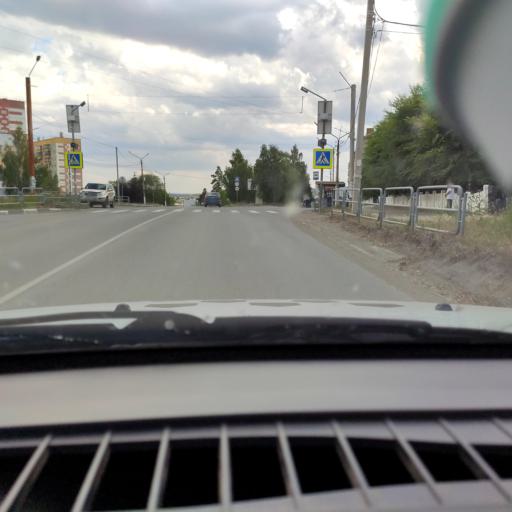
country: RU
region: Chelyabinsk
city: Miass
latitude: 55.0792
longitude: 60.0938
